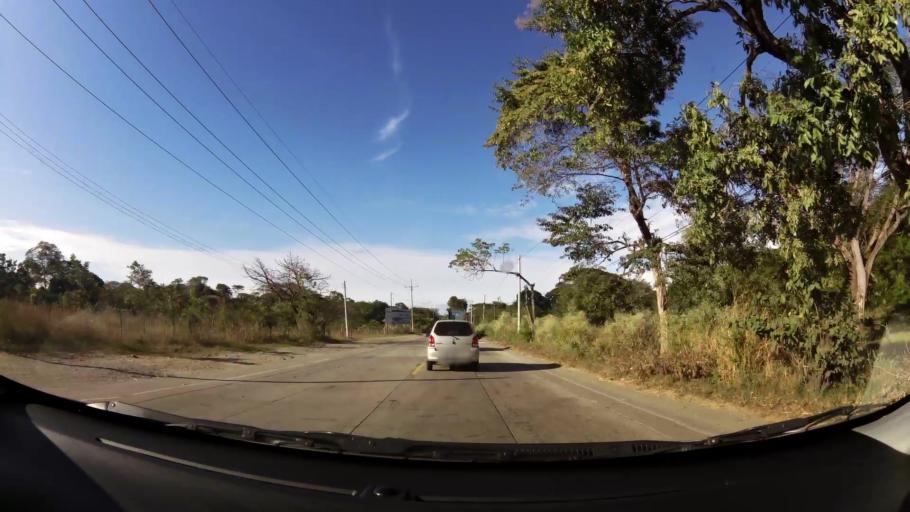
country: SV
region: Santa Ana
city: Metapan
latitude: 14.2818
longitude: -89.4615
